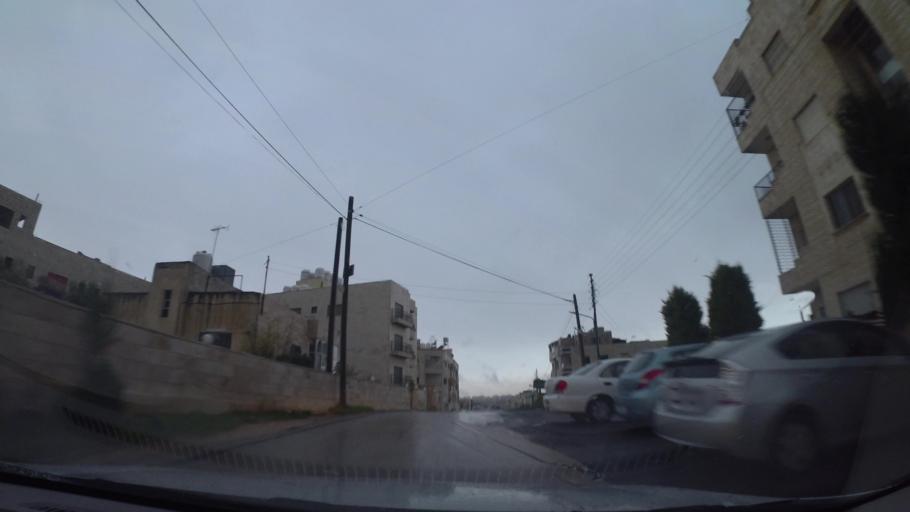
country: JO
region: Amman
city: Umm as Summaq
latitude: 31.9053
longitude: 35.8545
